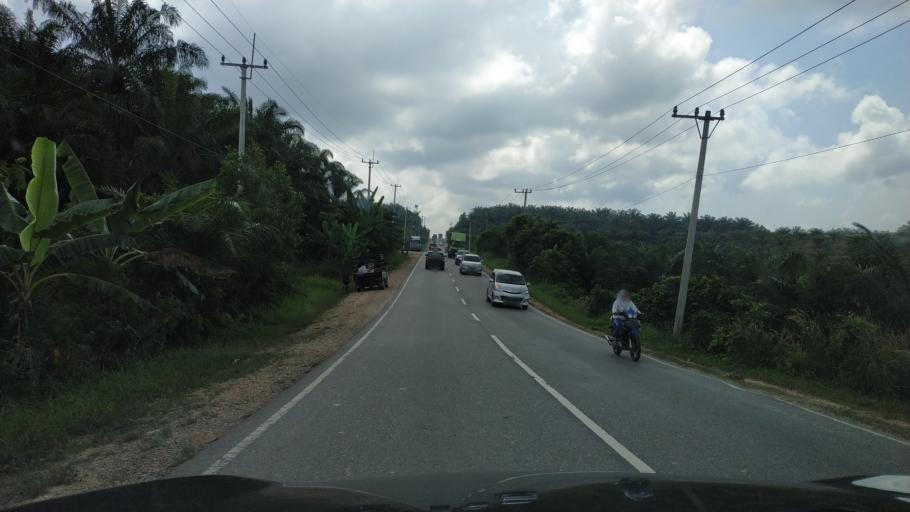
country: ID
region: Riau
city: Pangkalanbunut
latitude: 0.3012
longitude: 101.9172
